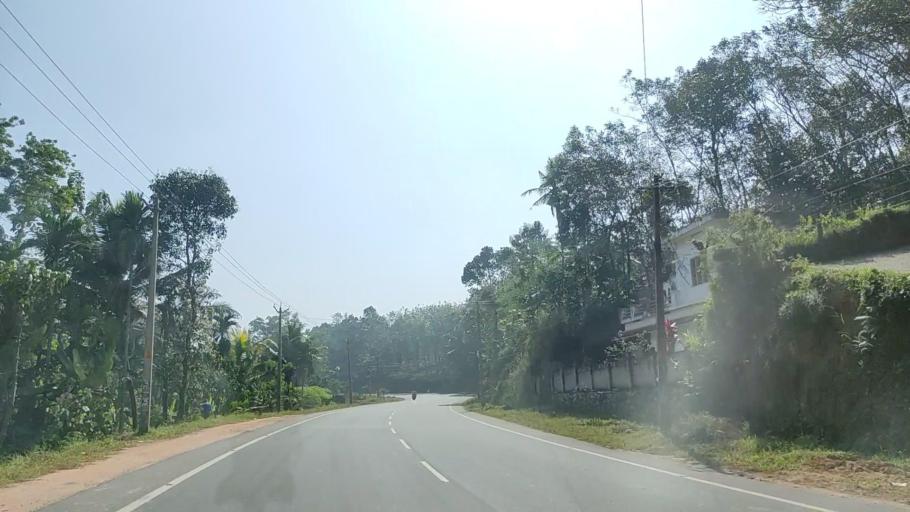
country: IN
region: Kerala
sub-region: Kollam
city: Punalur
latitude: 8.9316
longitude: 76.9668
